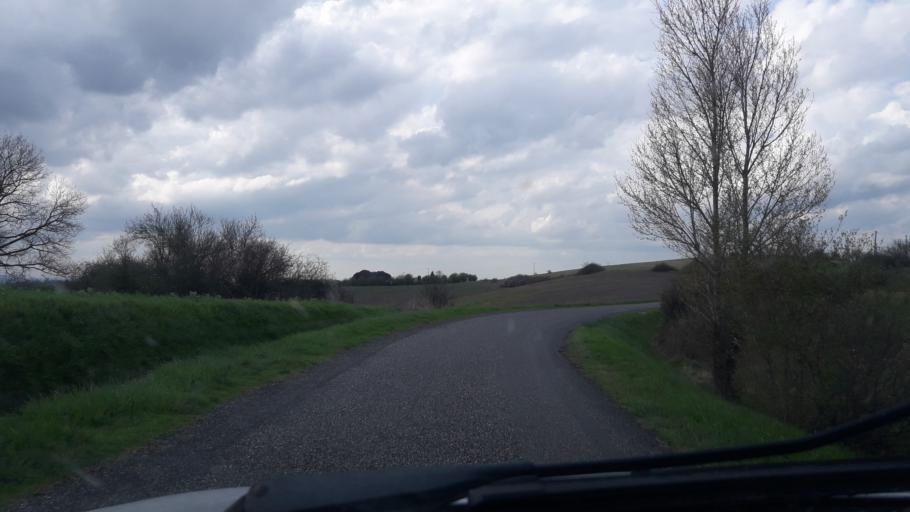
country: FR
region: Midi-Pyrenees
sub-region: Departement de l'Ariege
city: Lezat-sur-Leze
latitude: 43.1947
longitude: 1.3228
